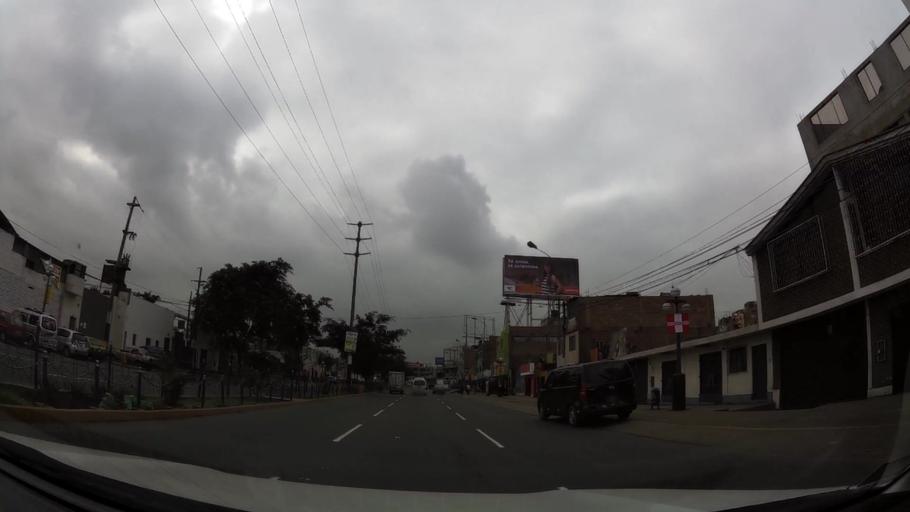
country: PE
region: Lima
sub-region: Lima
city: Surco
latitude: -12.1840
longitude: -77.0024
